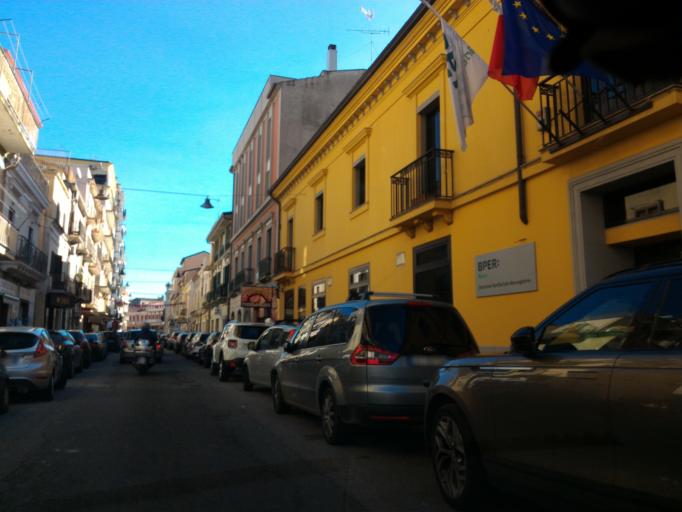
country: IT
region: Calabria
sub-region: Provincia di Crotone
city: Crotone
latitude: 39.0807
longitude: 17.1246
